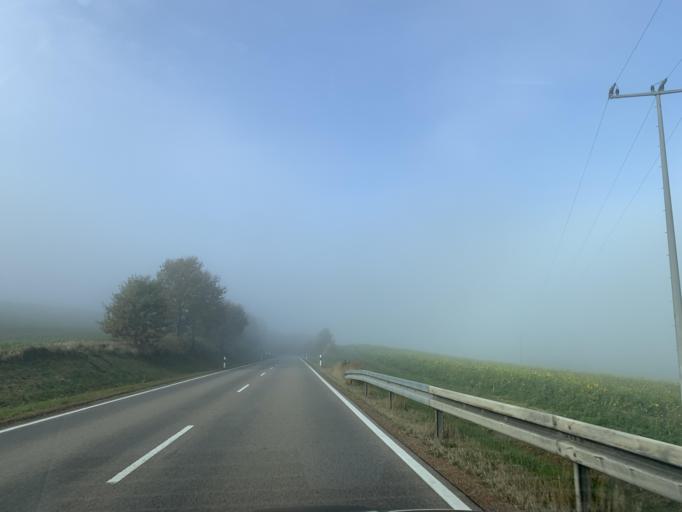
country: DE
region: Bavaria
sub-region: Upper Palatinate
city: Brunn
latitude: 49.2400
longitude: 12.1886
